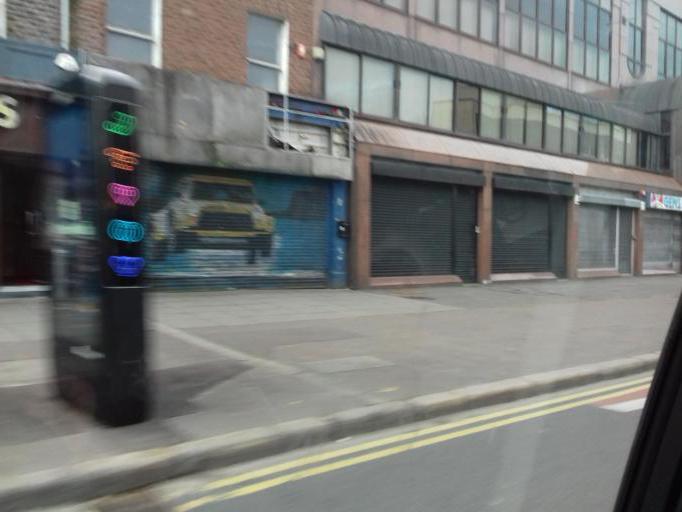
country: GB
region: Northern Ireland
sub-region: City of Belfast
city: Belfast
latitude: 54.5896
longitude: -5.9345
